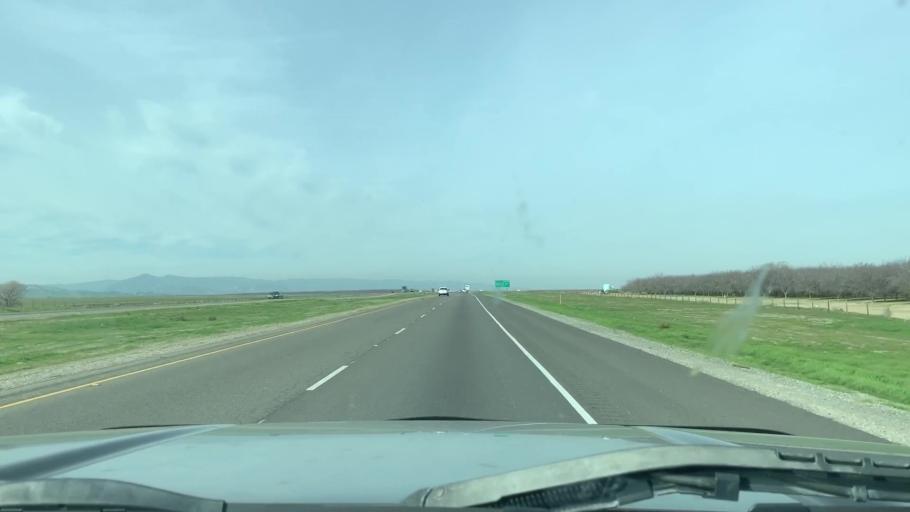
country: US
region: California
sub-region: Fresno County
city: Mendota
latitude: 36.5904
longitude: -120.5666
